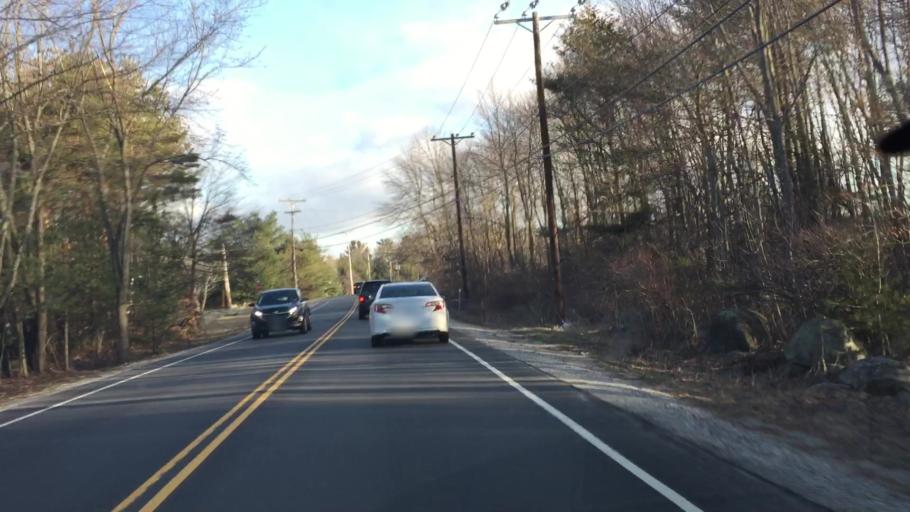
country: US
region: New Hampshire
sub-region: Rockingham County
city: Londonderry
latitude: 42.8203
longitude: -71.3627
